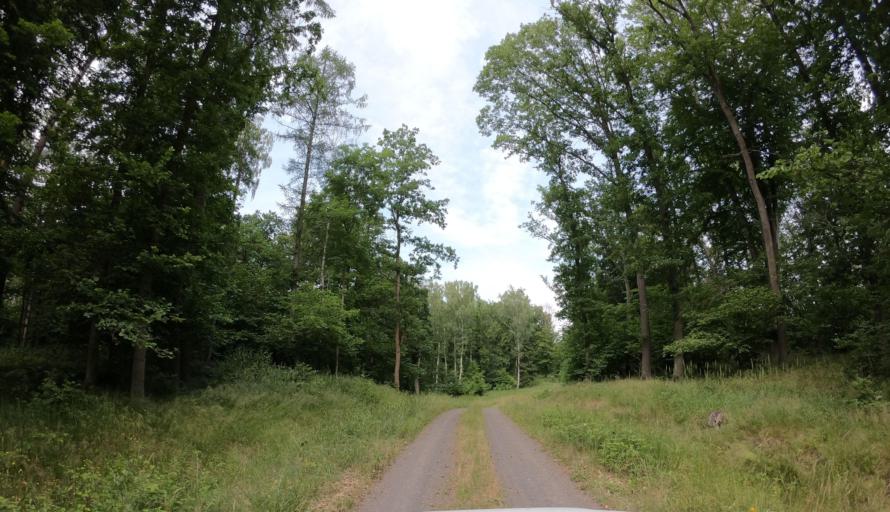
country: PL
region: West Pomeranian Voivodeship
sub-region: Powiat gryfinski
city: Banie
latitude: 53.0284
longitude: 14.7418
